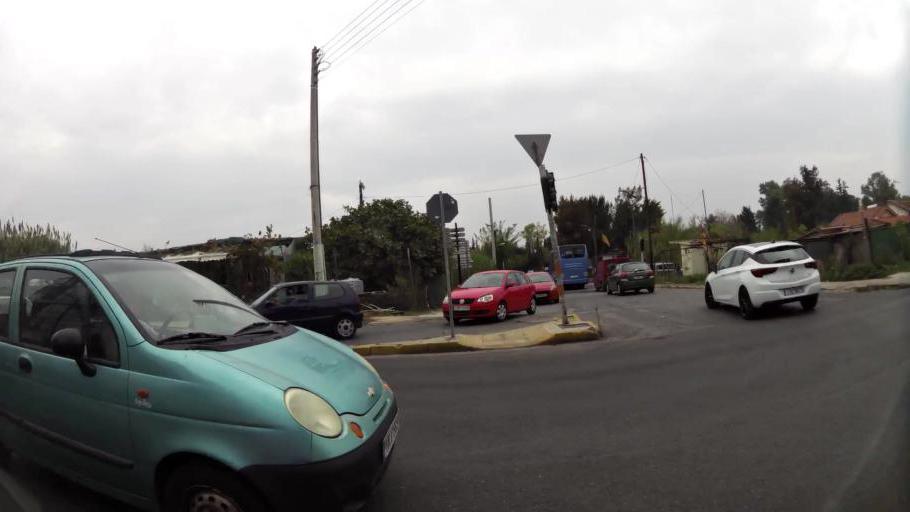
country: GR
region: Attica
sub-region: Nomarchia Athinas
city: Agioi Anargyroi
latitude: 38.0328
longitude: 23.7169
